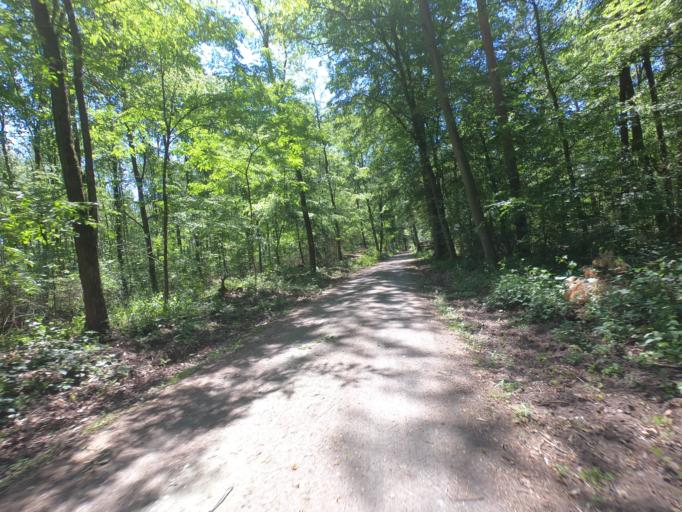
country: DE
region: Hesse
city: Niederrad
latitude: 50.0427
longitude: 8.6440
